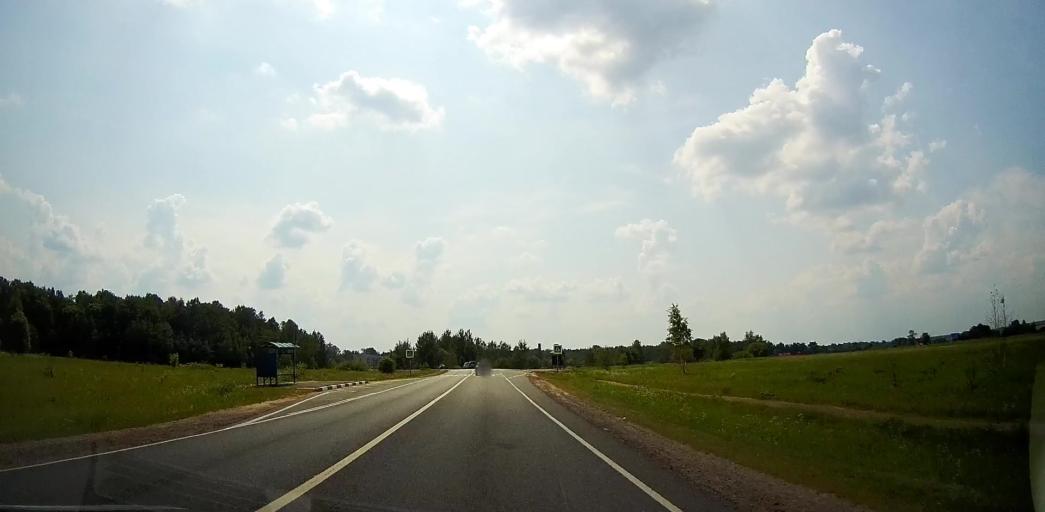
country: RU
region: Moskovskaya
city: Malino
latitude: 55.0970
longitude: 38.1660
